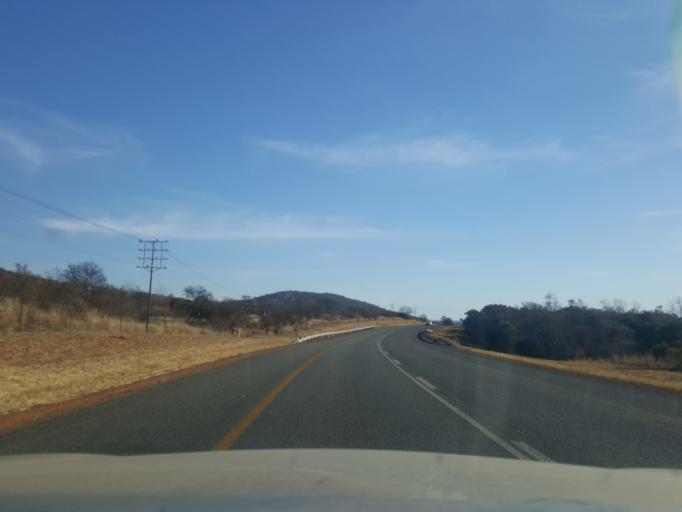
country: ZA
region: North-West
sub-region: Ngaka Modiri Molema District Municipality
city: Zeerust
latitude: -25.5360
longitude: 26.1304
